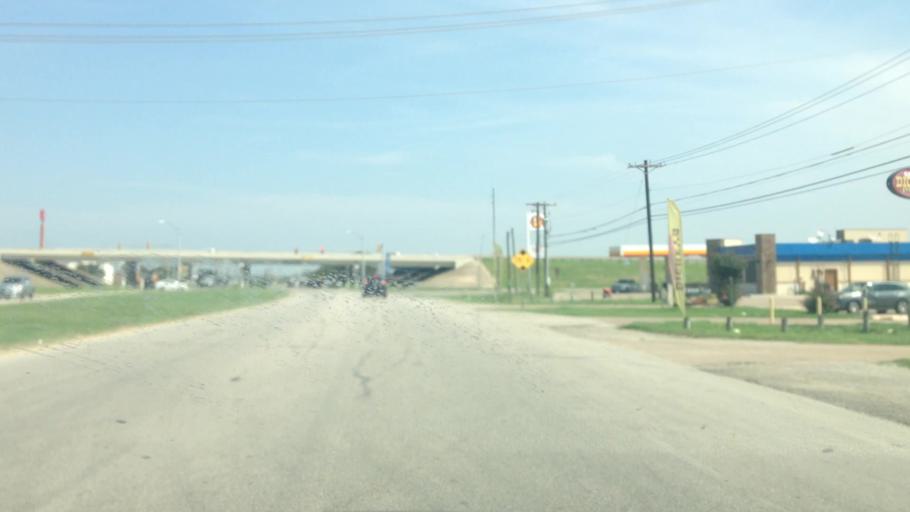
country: US
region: Texas
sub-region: Tarrant County
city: Blue Mound
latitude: 32.8410
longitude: -97.3429
